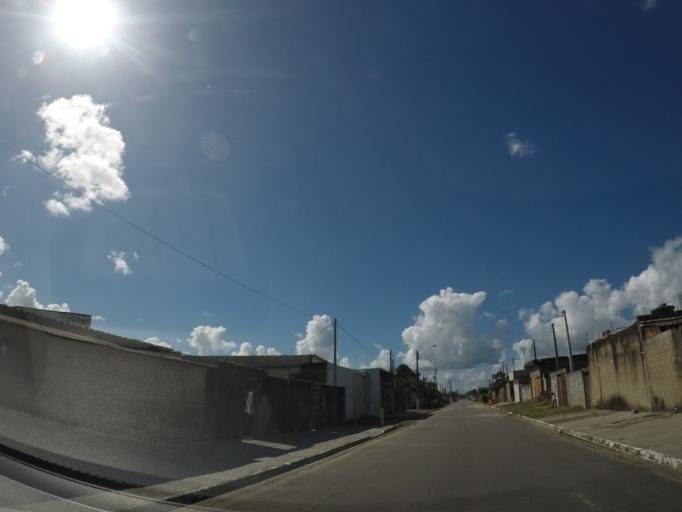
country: BR
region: Sao Paulo
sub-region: Praia Grande
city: Praia Grande
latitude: -24.0174
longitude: -46.5140
